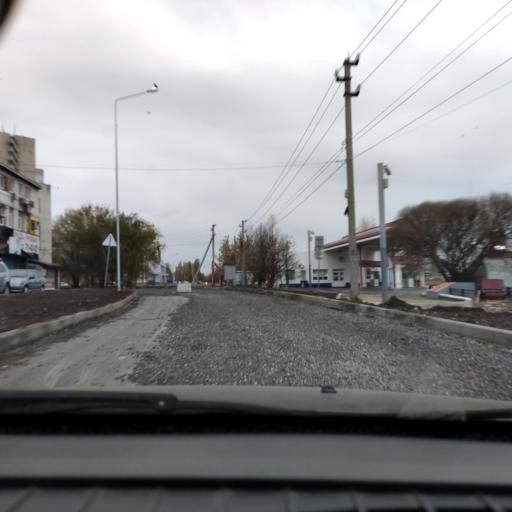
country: RU
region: Samara
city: Tol'yatti
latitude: 53.5442
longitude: 49.3214
